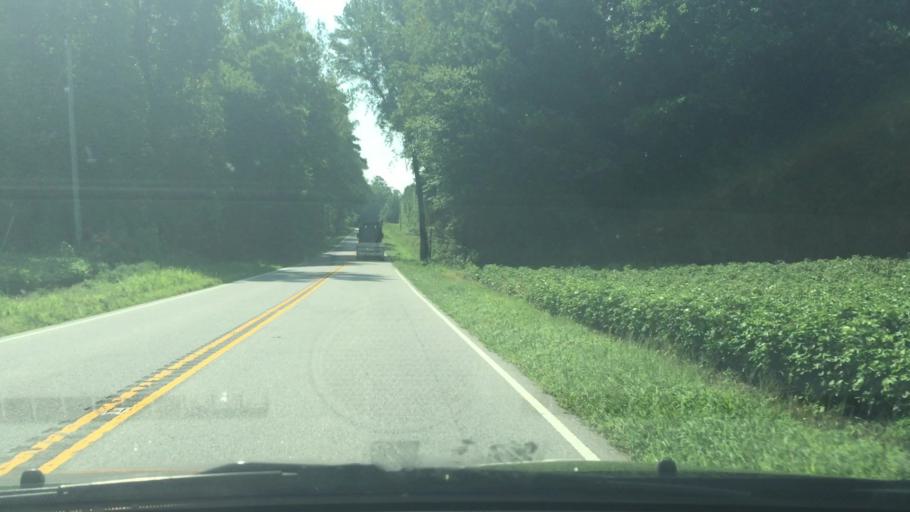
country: US
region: Virginia
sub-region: Sussex County
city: Sussex
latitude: 36.8723
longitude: -77.1458
